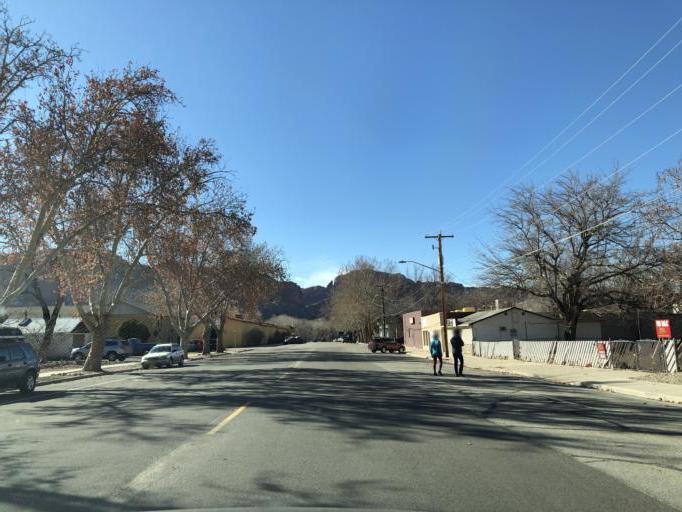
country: US
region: Utah
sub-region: Grand County
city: Moab
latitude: 38.5717
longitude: -109.5475
